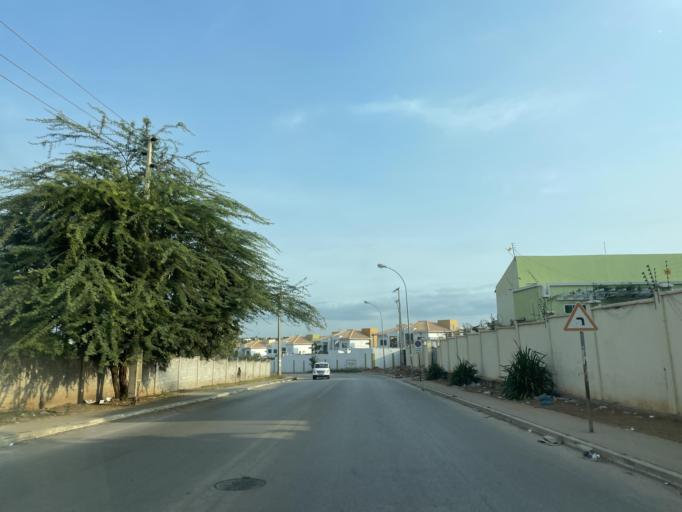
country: AO
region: Luanda
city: Luanda
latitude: -8.9168
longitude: 13.2037
